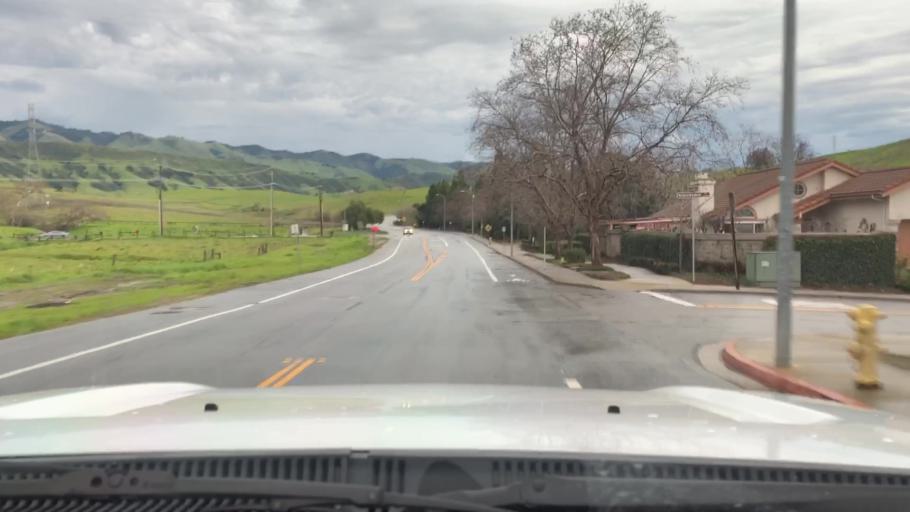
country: US
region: California
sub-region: San Luis Obispo County
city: San Luis Obispo
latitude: 35.2503
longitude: -120.6271
